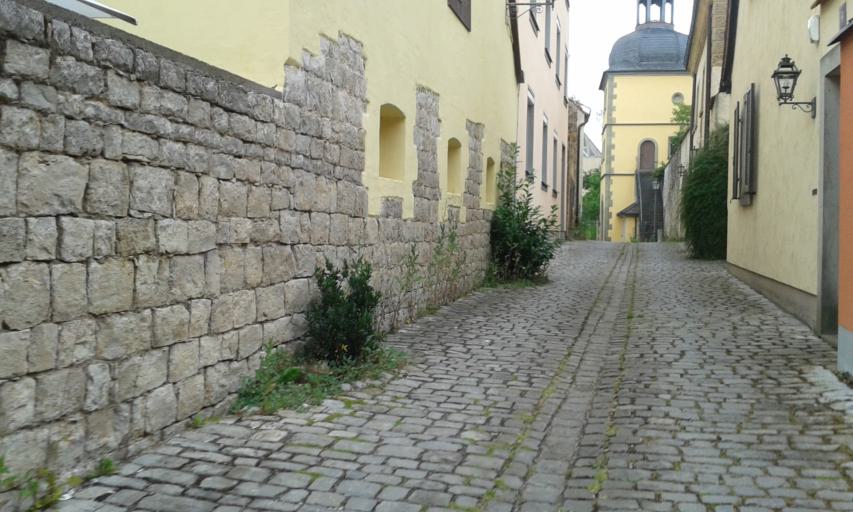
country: DE
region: Bavaria
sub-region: Regierungsbezirk Unterfranken
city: Hassfurt
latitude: 50.0304
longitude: 10.5073
